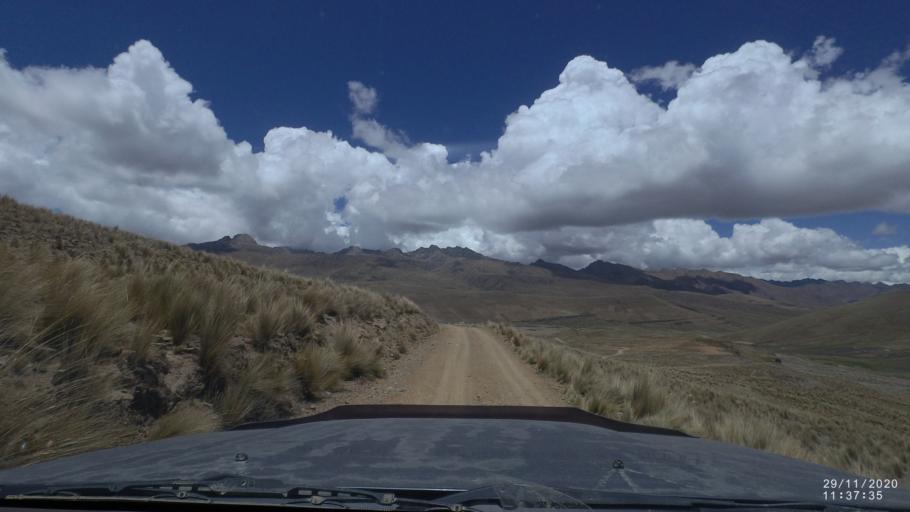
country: BO
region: Cochabamba
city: Cochabamba
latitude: -17.1975
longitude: -66.2332
